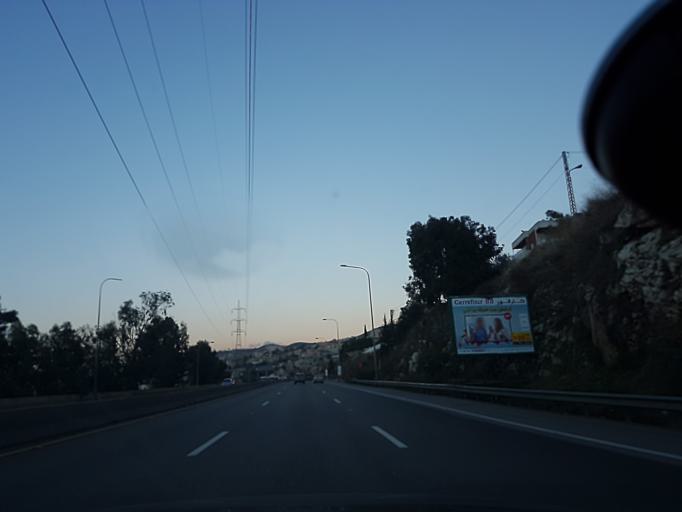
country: LB
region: Liban-Sud
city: Sidon
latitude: 33.6522
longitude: 35.4196
